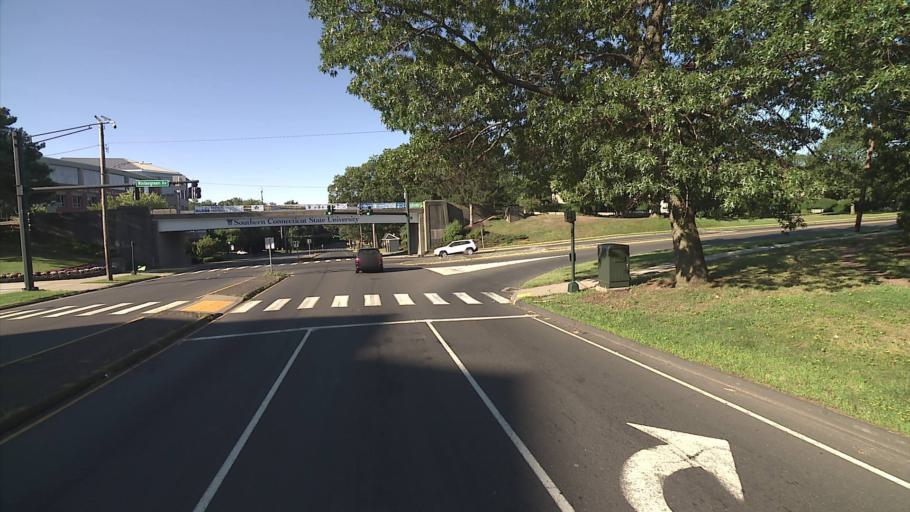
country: US
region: Connecticut
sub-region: New Haven County
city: New Haven
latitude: 41.3332
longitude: -72.9491
